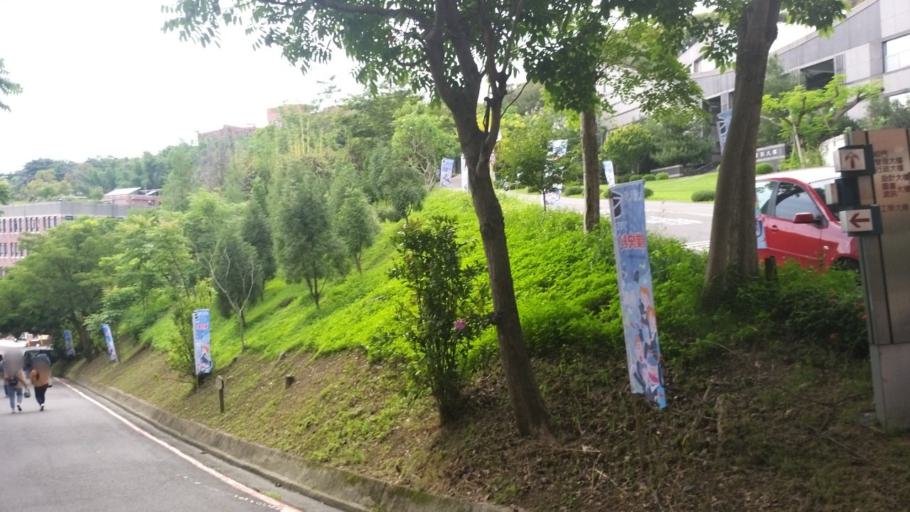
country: TW
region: Taiwan
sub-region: Changhua
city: Chang-hua
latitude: 24.0008
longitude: 120.5984
